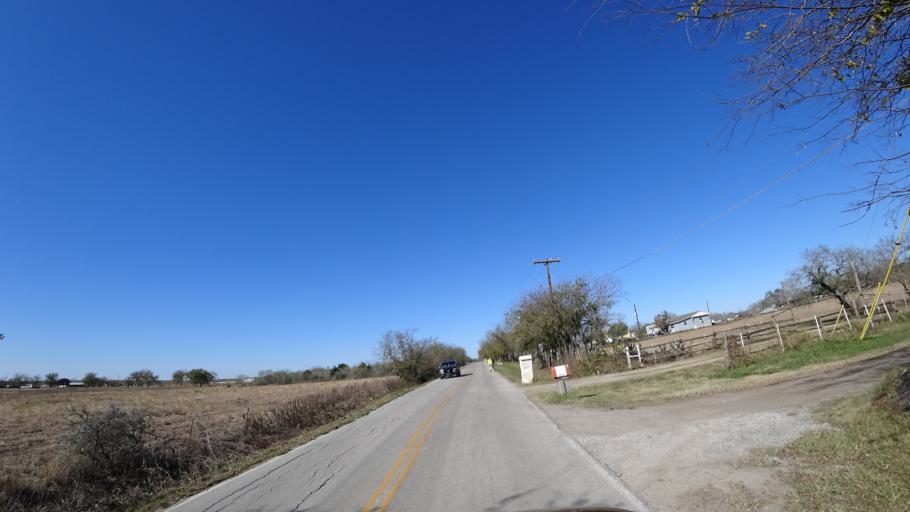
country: US
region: Texas
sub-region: Travis County
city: Garfield
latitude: 30.1197
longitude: -97.5941
